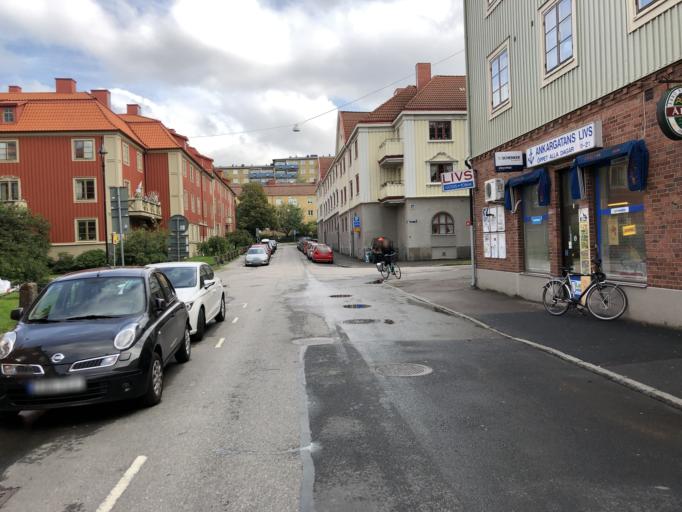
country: SE
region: Vaestra Goetaland
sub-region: Goteborg
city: Majorna
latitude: 57.6936
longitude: 11.9273
